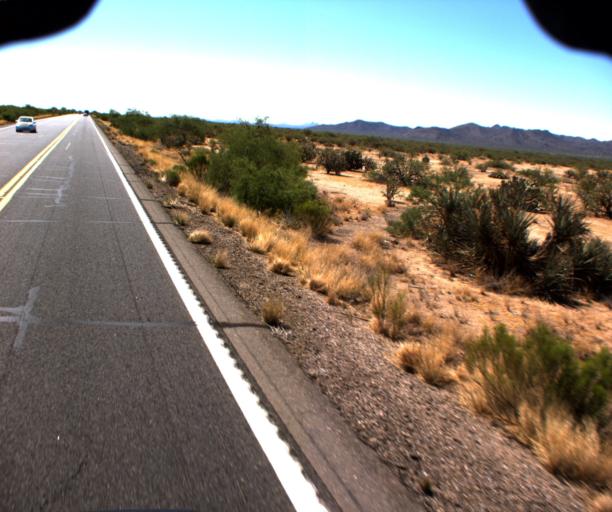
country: US
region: Arizona
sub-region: Yavapai County
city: Congress
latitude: 34.1392
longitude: -112.9733
